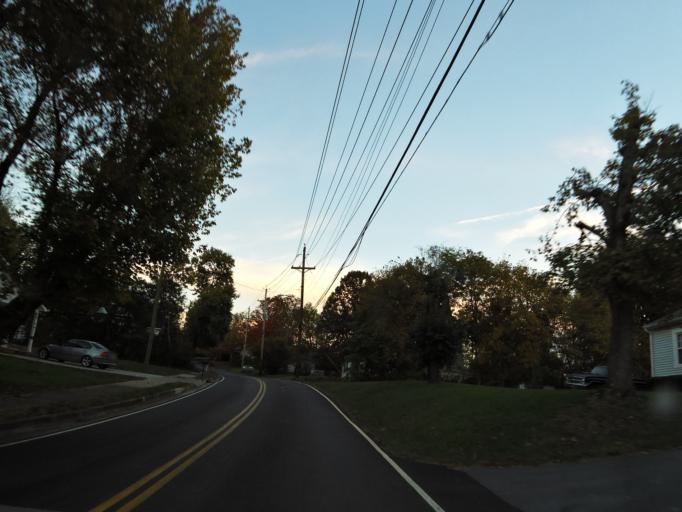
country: US
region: Tennessee
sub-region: Knox County
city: Knoxville
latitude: 35.9378
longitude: -83.9141
